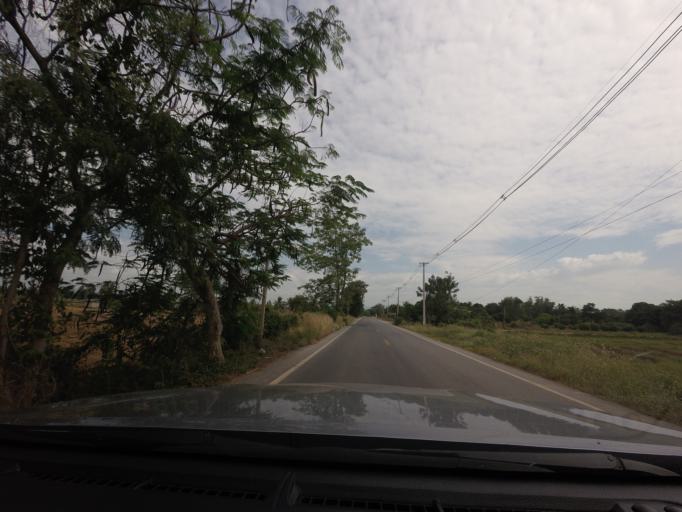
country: TH
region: Phitsanulok
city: Wang Thong
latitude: 16.7227
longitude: 100.3499
